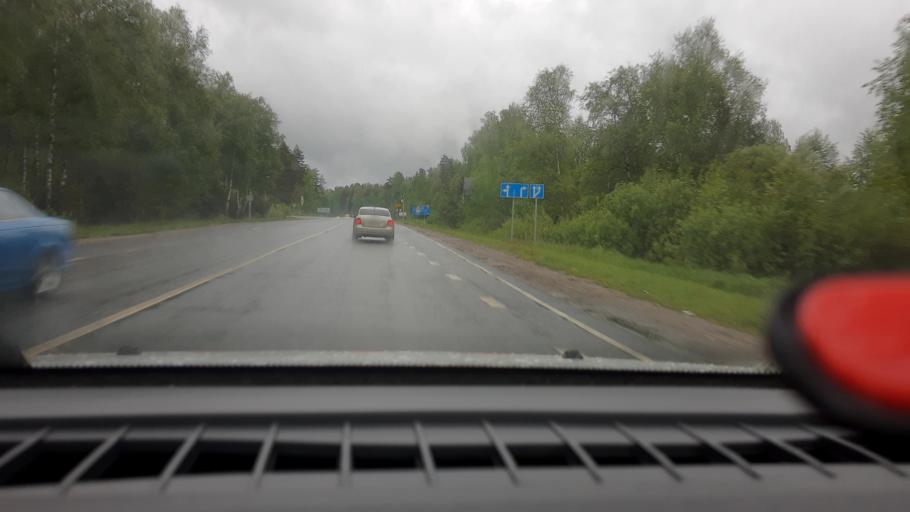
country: RU
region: Nizjnij Novgorod
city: Linda
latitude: 56.6335
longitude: 44.0968
